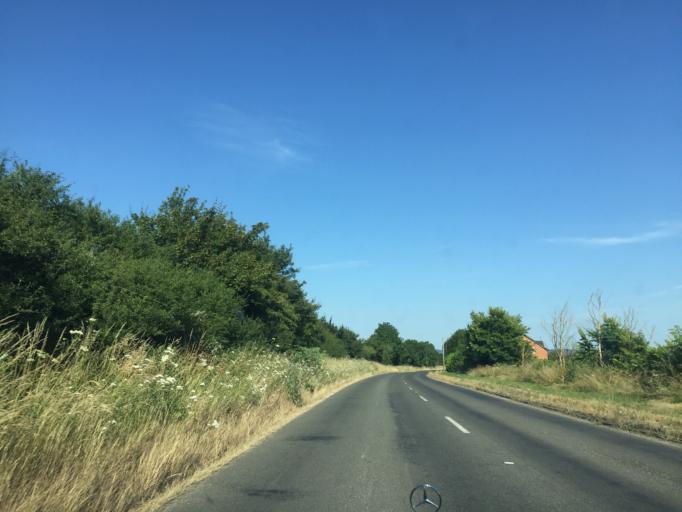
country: GB
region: England
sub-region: Buckinghamshire
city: Long Crendon
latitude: 51.7222
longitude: -1.0379
